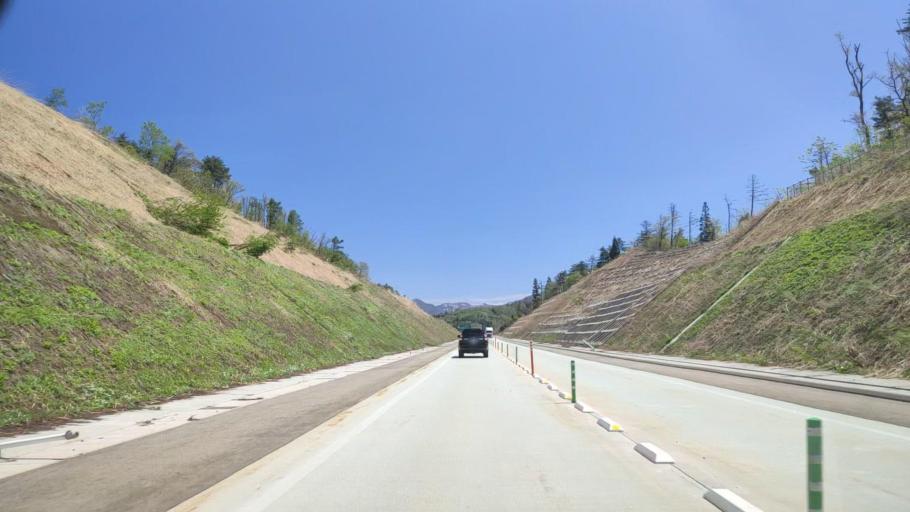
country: JP
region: Yamagata
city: Obanazawa
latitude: 38.5858
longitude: 140.3930
